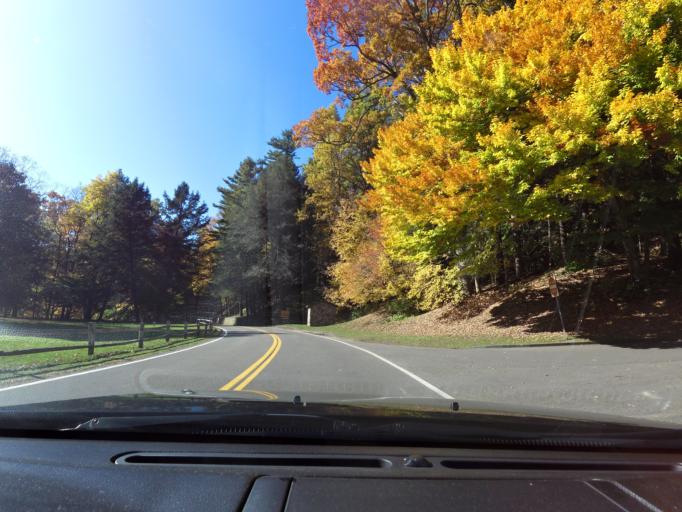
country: US
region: New York
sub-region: Wyoming County
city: Castile
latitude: 42.5849
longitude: -78.0445
